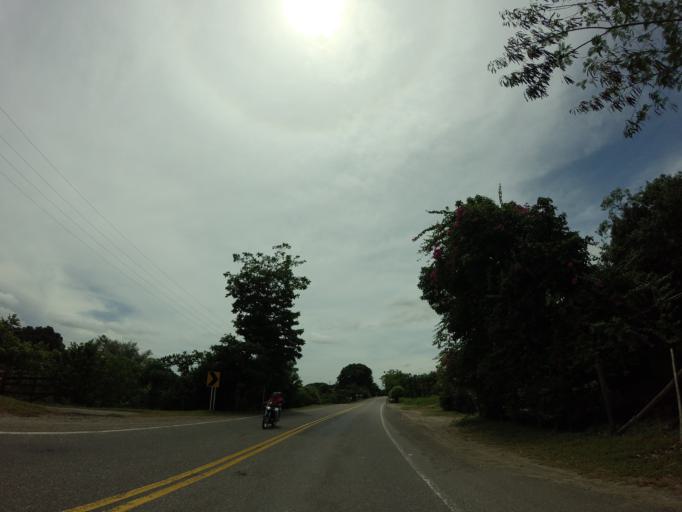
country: CO
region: Caldas
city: La Dorada
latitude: 5.4207
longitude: -74.6855
